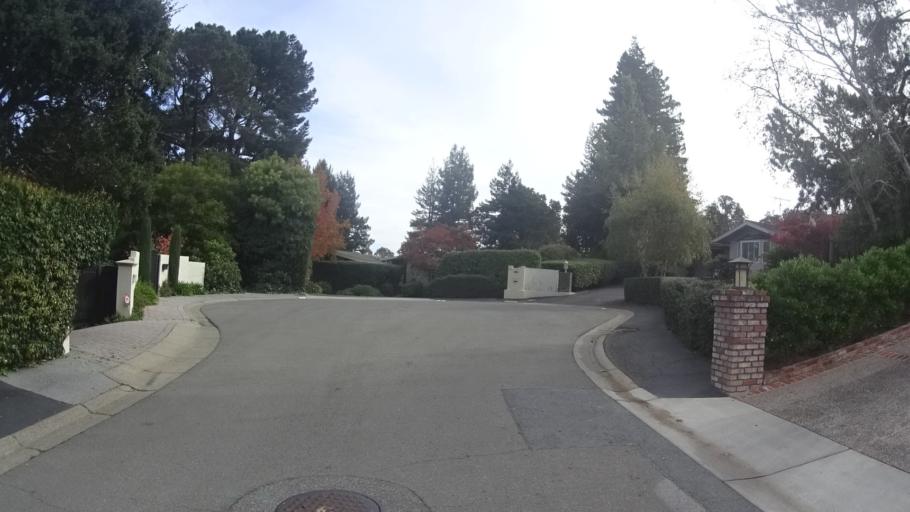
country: US
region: California
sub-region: San Mateo County
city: Hillsborough
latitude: 37.5703
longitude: -122.3842
